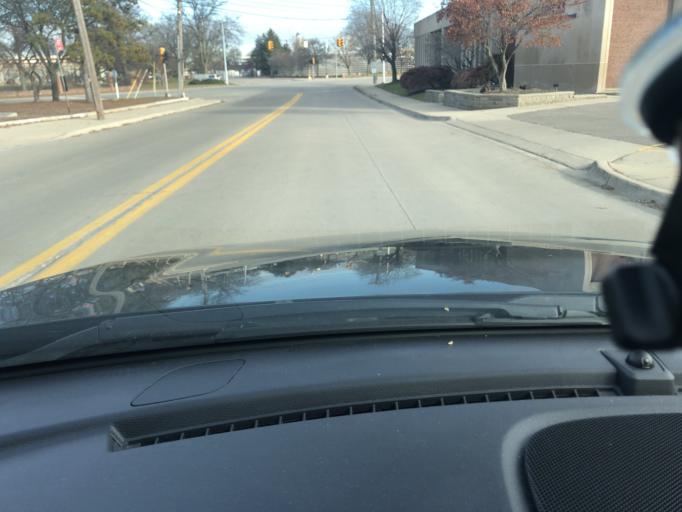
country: US
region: Michigan
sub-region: Wayne County
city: Dearborn Heights
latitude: 42.3025
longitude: -83.2405
